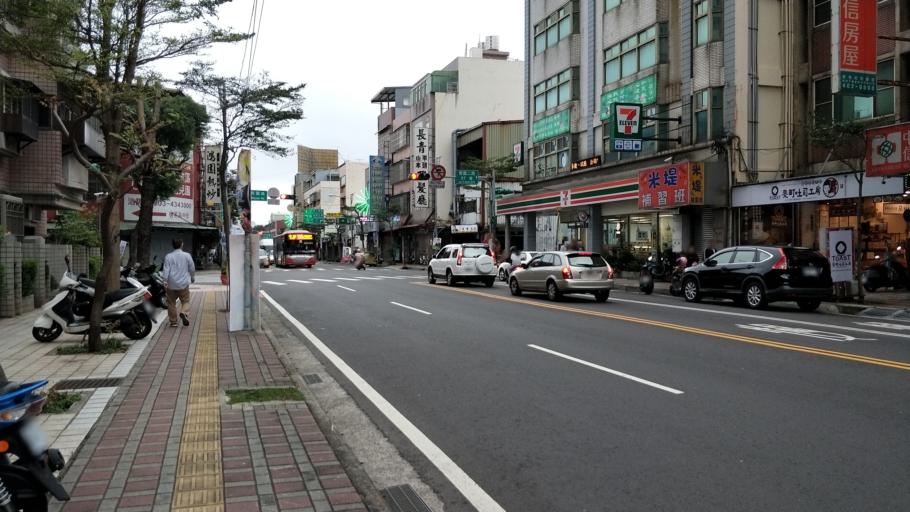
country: TW
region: Taiwan
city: Taoyuan City
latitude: 24.9716
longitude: 121.2341
